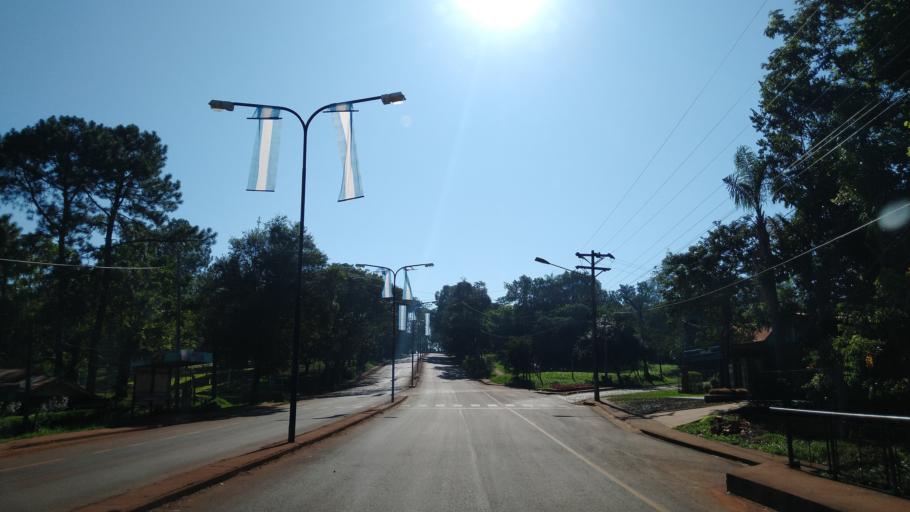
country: AR
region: Misiones
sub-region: Departamento de Montecarlo
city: Montecarlo
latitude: -26.5710
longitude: -54.7292
